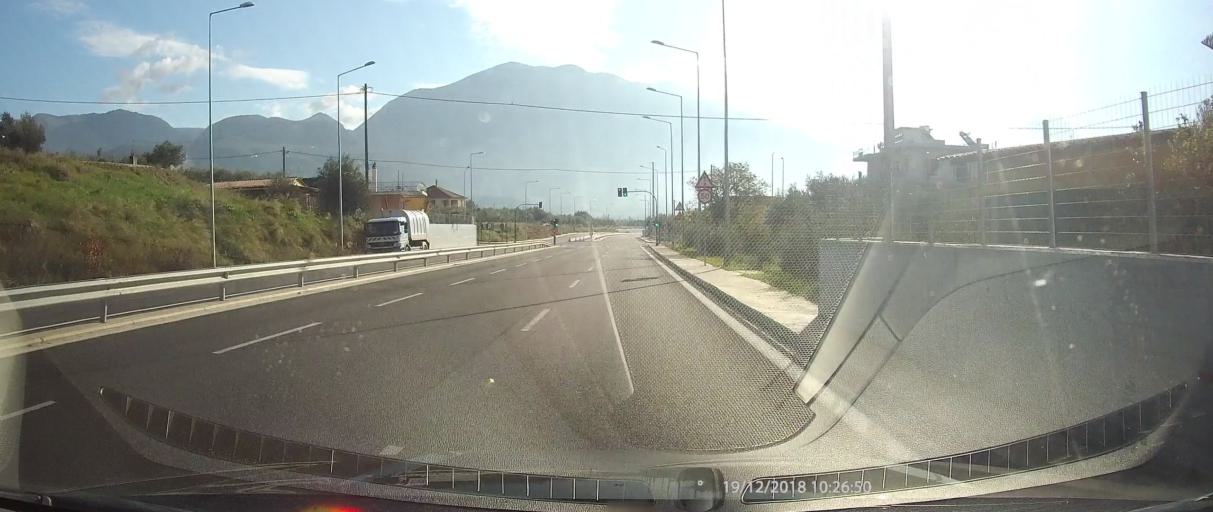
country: GR
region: Peloponnese
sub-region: Nomos Messinias
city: Kalamata
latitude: 37.0421
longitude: 22.1312
